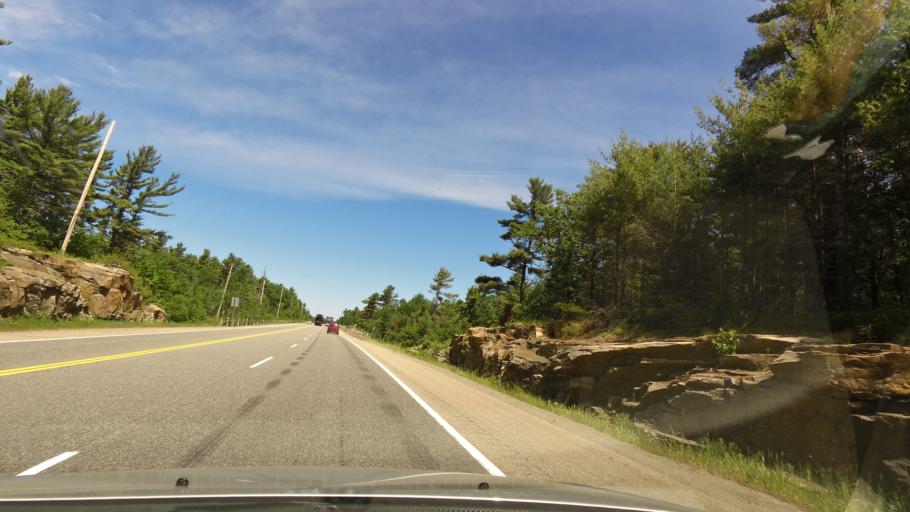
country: CA
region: Ontario
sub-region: Parry Sound District
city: Parry Sound
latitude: 45.6183
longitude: -80.3846
